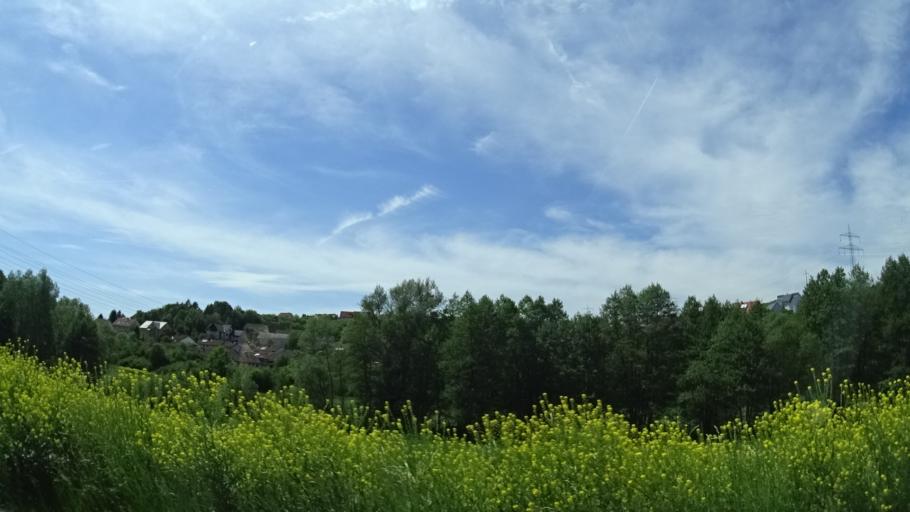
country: DE
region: Bavaria
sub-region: Regierungsbezirk Unterfranken
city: Arnstein
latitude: 49.9843
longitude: 9.9760
